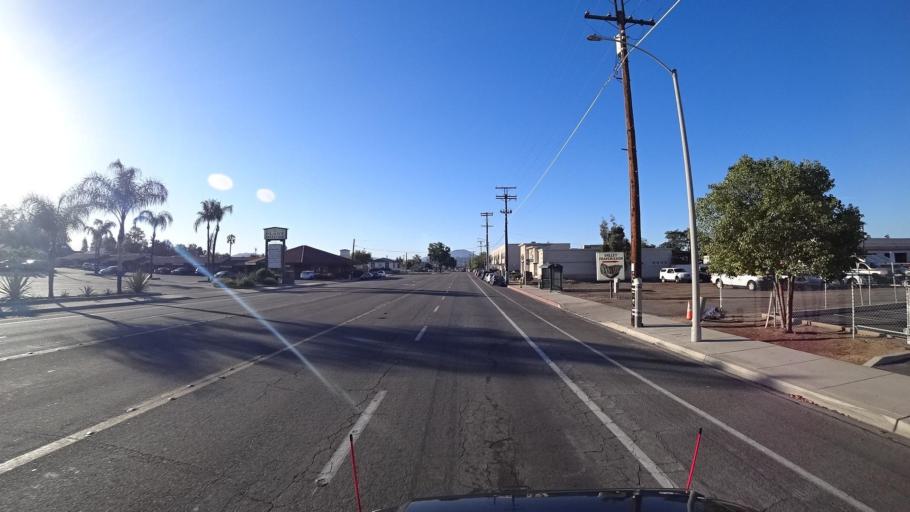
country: US
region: California
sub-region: San Diego County
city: Bostonia
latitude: 32.8111
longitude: -116.9358
